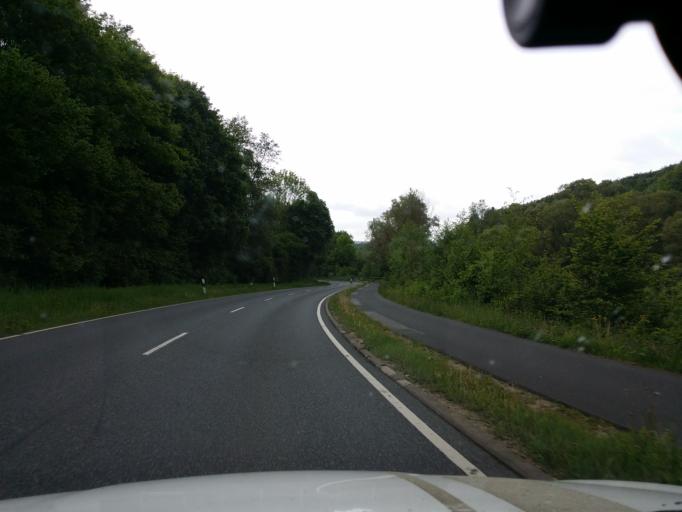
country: DE
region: Hesse
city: Eppstein
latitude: 50.1662
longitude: 8.3765
